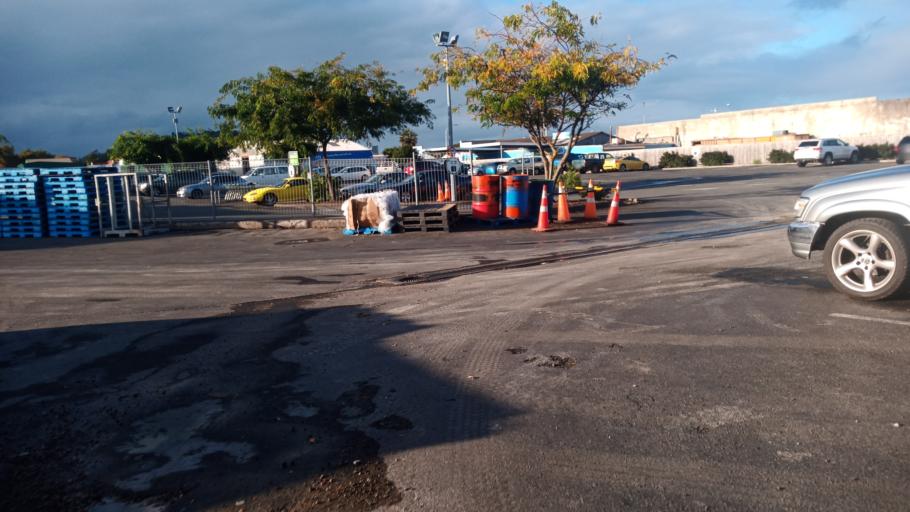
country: NZ
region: Gisborne
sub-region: Gisborne District
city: Gisborne
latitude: -38.6613
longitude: 178.0177
